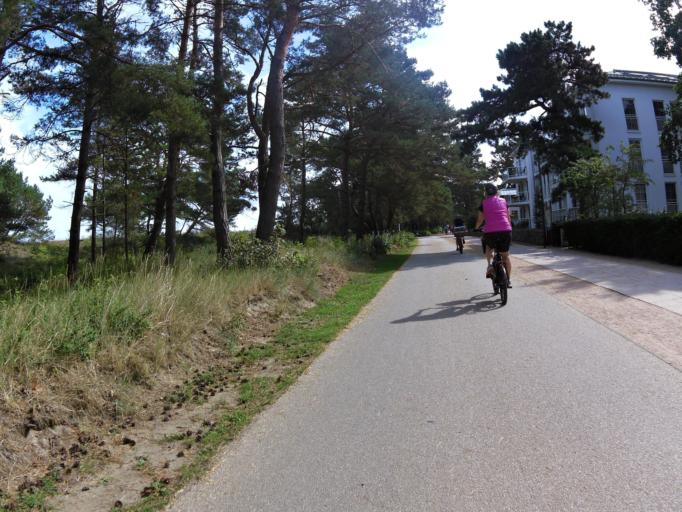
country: DE
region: Mecklenburg-Vorpommern
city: Seebad Bansin
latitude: 53.9668
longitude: 14.1528
